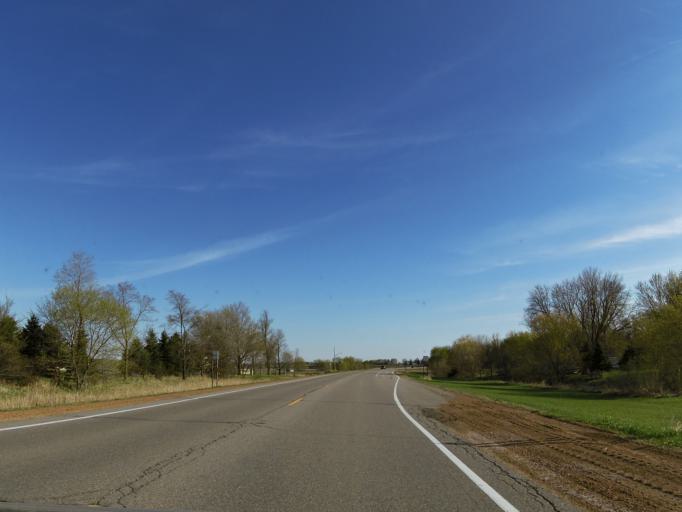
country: US
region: Minnesota
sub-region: Scott County
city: Prior Lake
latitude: 44.6544
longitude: -93.4996
